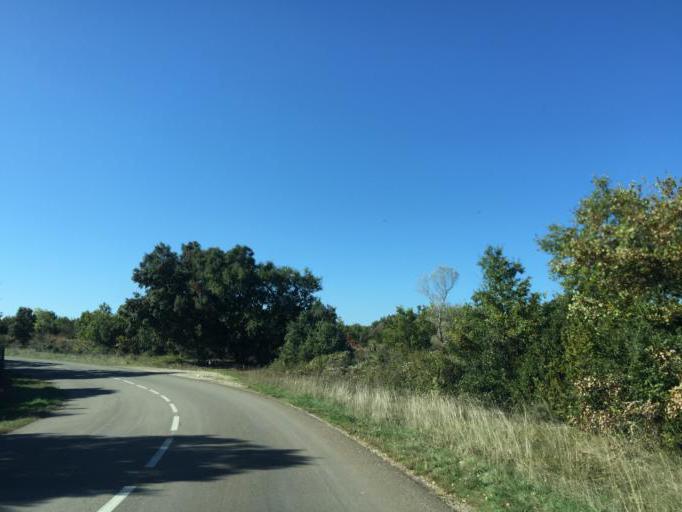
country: FR
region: Rhone-Alpes
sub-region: Departement de l'Ardeche
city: Bourg-Saint-Andeol
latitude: 44.4367
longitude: 4.5742
